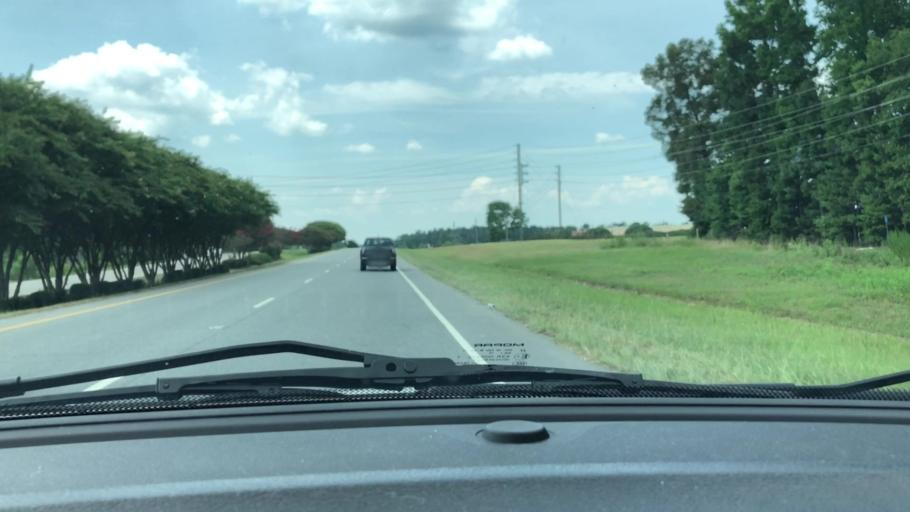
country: US
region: North Carolina
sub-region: Chatham County
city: Farmville
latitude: 35.5190
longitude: -79.2194
